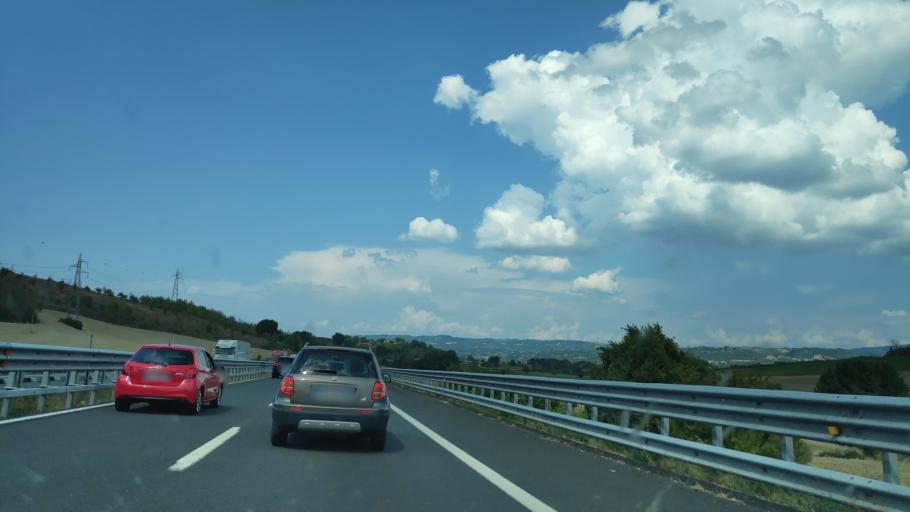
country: IT
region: Umbria
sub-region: Provincia di Terni
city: Fabro Scalo
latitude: 42.8466
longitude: 12.0391
